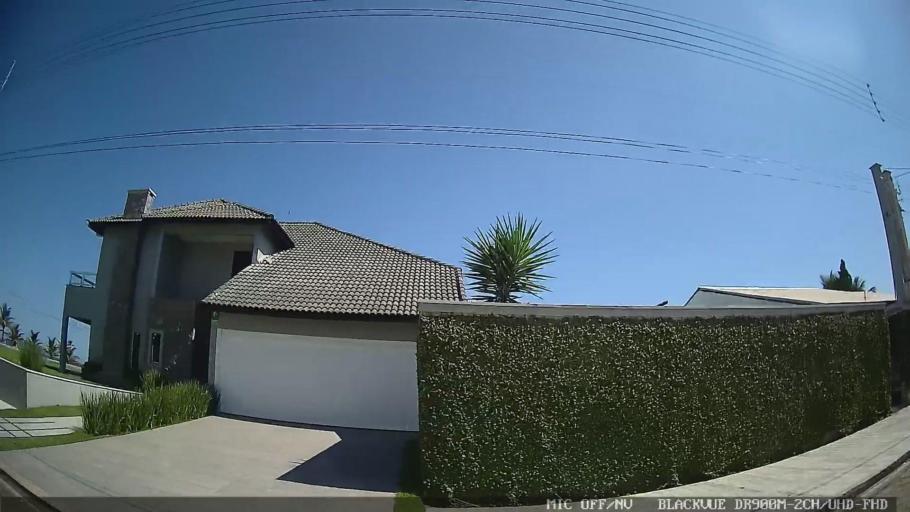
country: BR
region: Sao Paulo
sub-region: Peruibe
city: Peruibe
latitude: -24.2977
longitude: -46.9656
